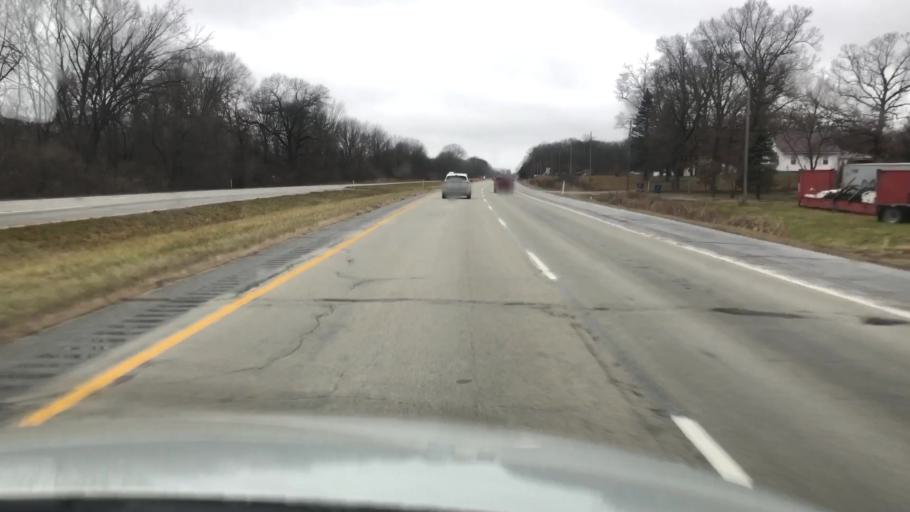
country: US
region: Indiana
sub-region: Starke County
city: Koontz Lake
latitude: 41.3649
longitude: -86.4672
